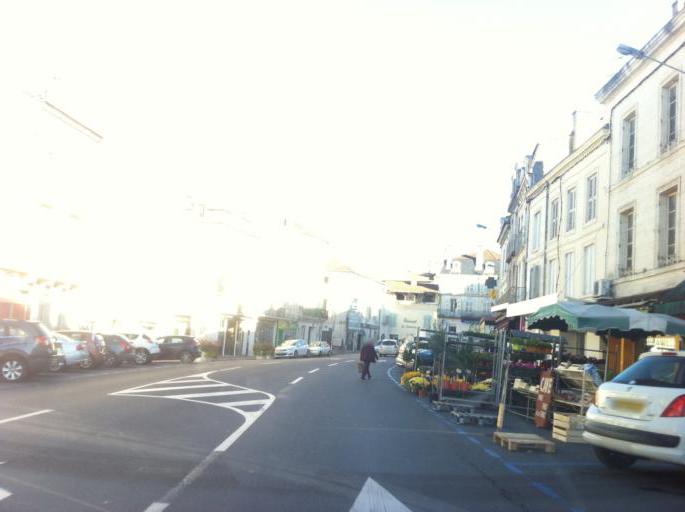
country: FR
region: Aquitaine
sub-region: Departement de la Dordogne
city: Riberac
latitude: 45.2471
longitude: 0.3401
